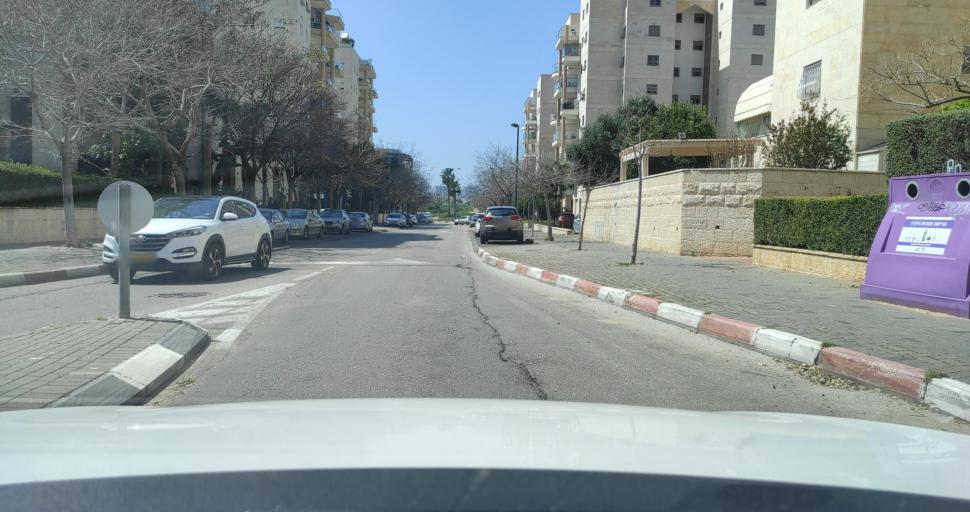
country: IL
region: Central District
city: Nordiyya
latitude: 32.2978
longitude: 34.8713
